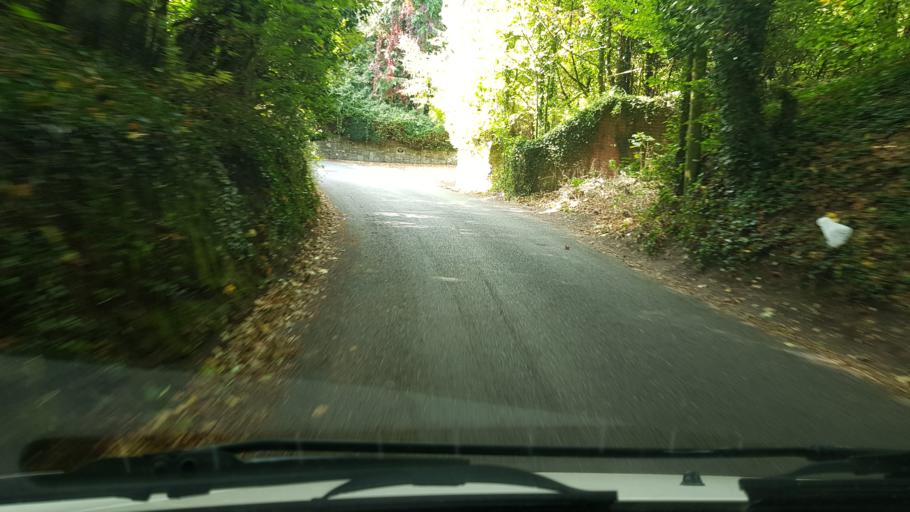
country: GB
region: England
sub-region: Surrey
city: Godalming
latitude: 51.2224
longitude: -0.6294
